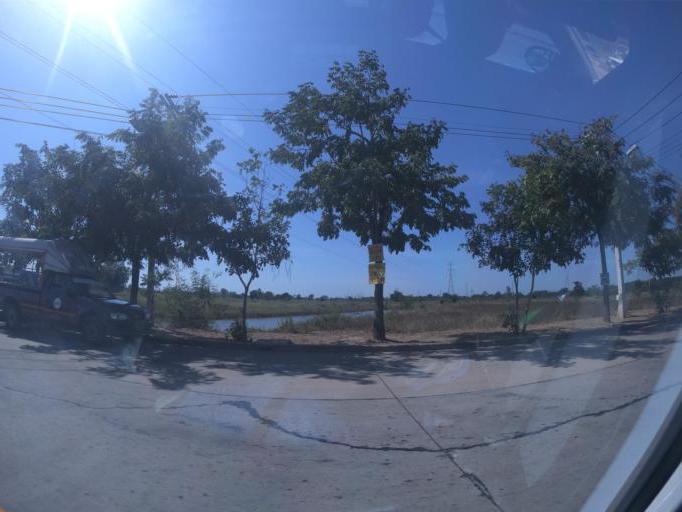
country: TH
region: Khon Kaen
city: Khon Kaen
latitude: 16.3896
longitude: 102.8029
